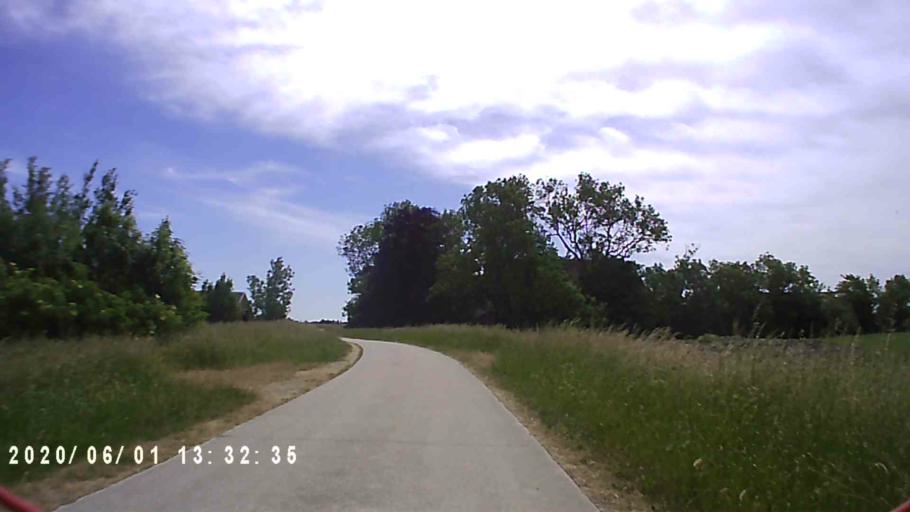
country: NL
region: Friesland
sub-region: Gemeente Littenseradiel
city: Wommels
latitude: 53.0928
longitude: 5.5686
